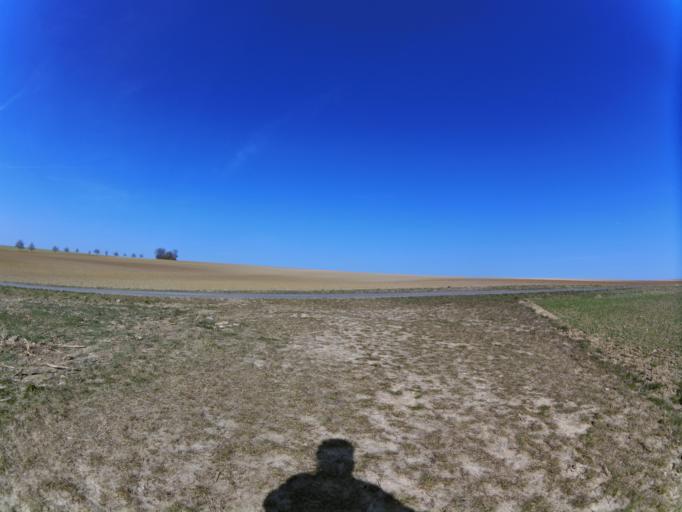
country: DE
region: Bavaria
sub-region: Regierungsbezirk Unterfranken
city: Prosselsheim
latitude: 49.8272
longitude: 10.1286
